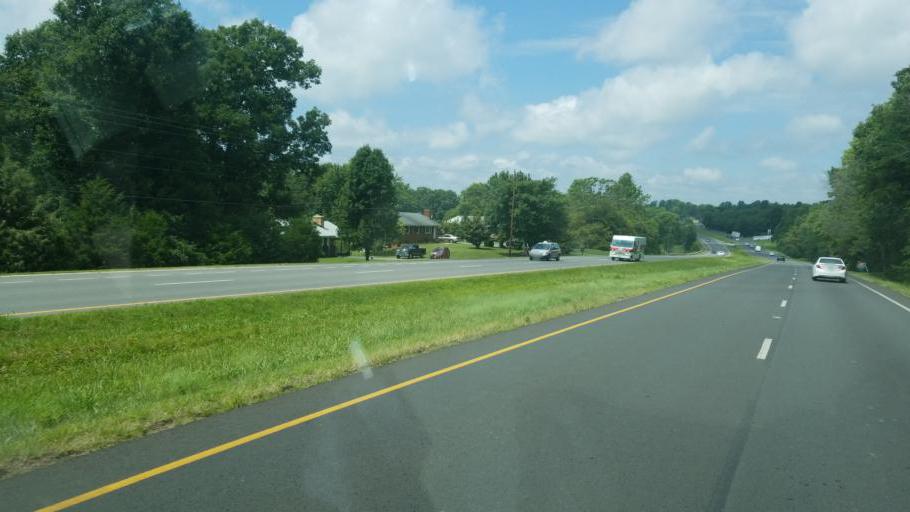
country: US
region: Virginia
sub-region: Fauquier County
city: Bealeton
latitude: 38.4945
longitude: -77.6865
